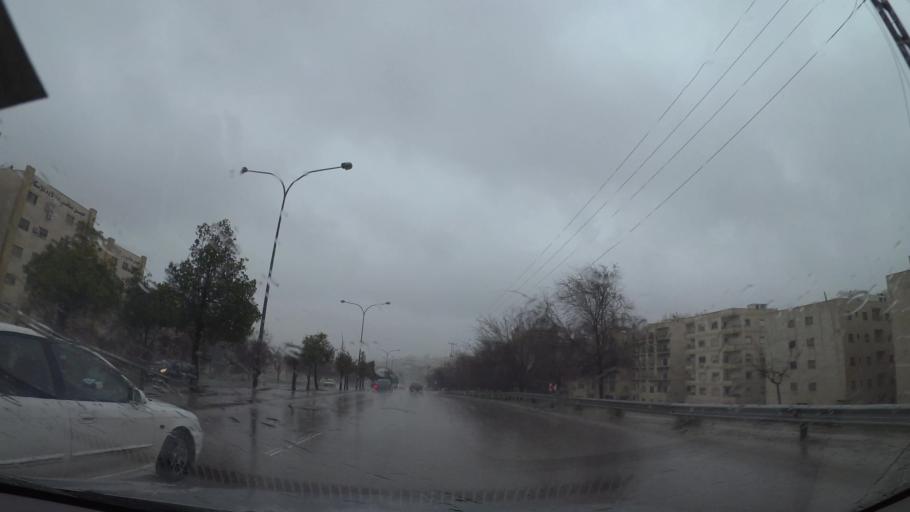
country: JO
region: Amman
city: Al Jubayhah
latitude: 32.0239
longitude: 35.8925
